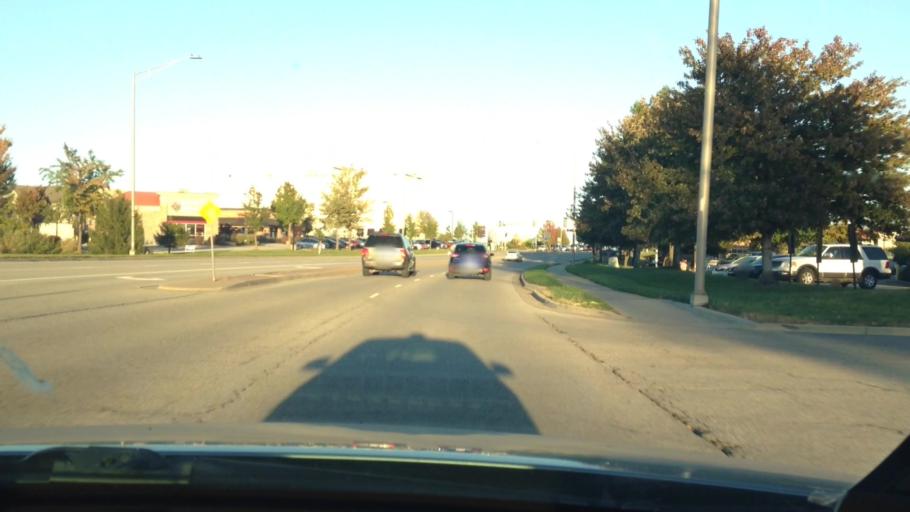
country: US
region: Kansas
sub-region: Johnson County
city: Olathe
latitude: 38.9098
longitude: -94.7729
